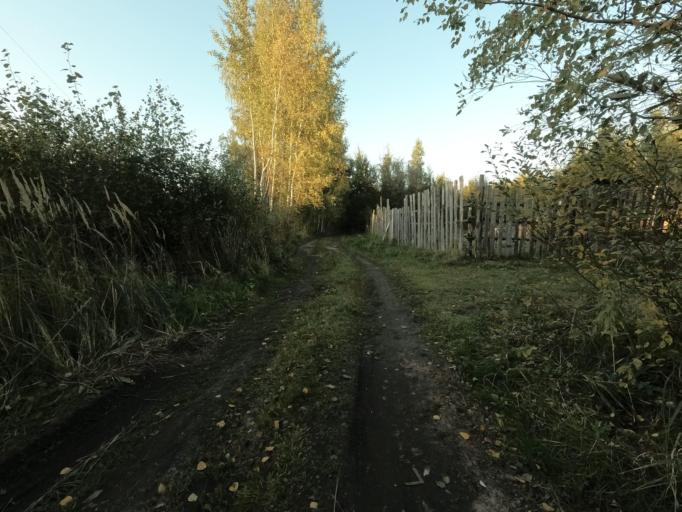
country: RU
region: Leningrad
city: Nikol'skoye
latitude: 59.7128
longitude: 30.7976
